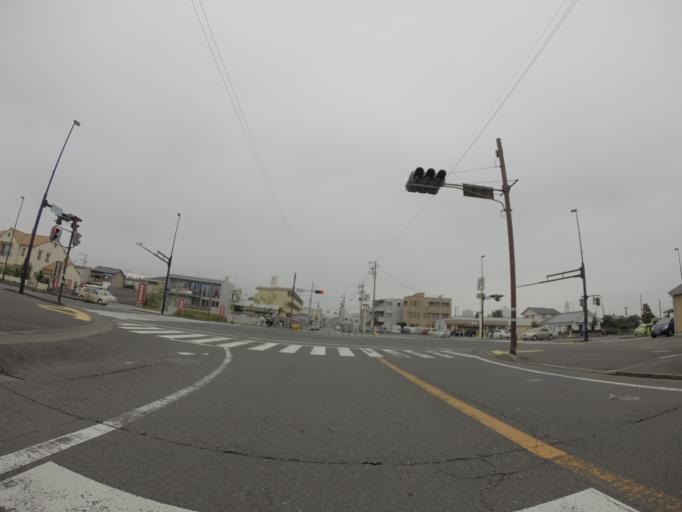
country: JP
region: Shizuoka
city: Shizuoka-shi
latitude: 34.9597
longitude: 138.3900
